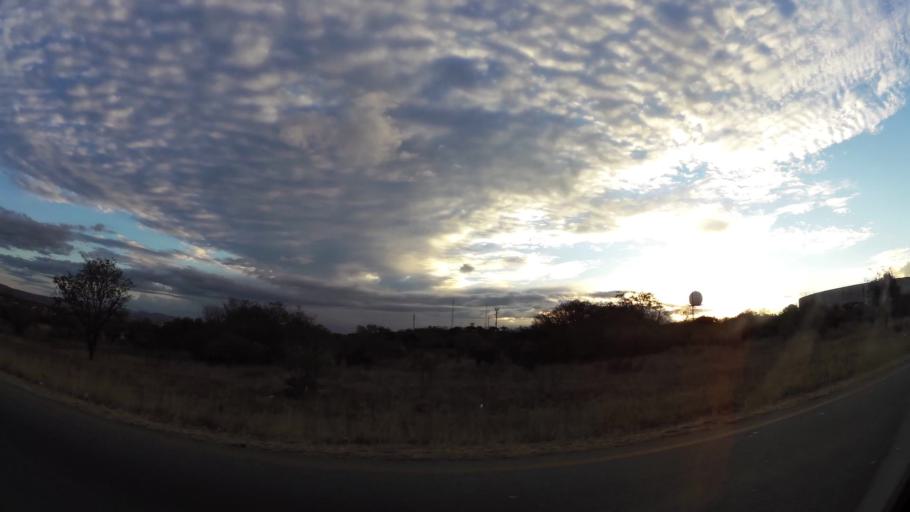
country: ZA
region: Limpopo
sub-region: Capricorn District Municipality
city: Polokwane
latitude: -23.8950
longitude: 29.5086
